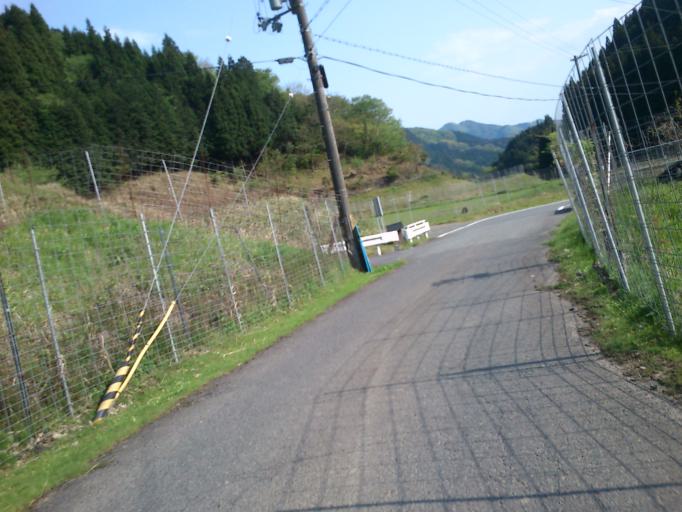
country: JP
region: Kyoto
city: Fukuchiyama
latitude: 35.3803
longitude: 135.0105
